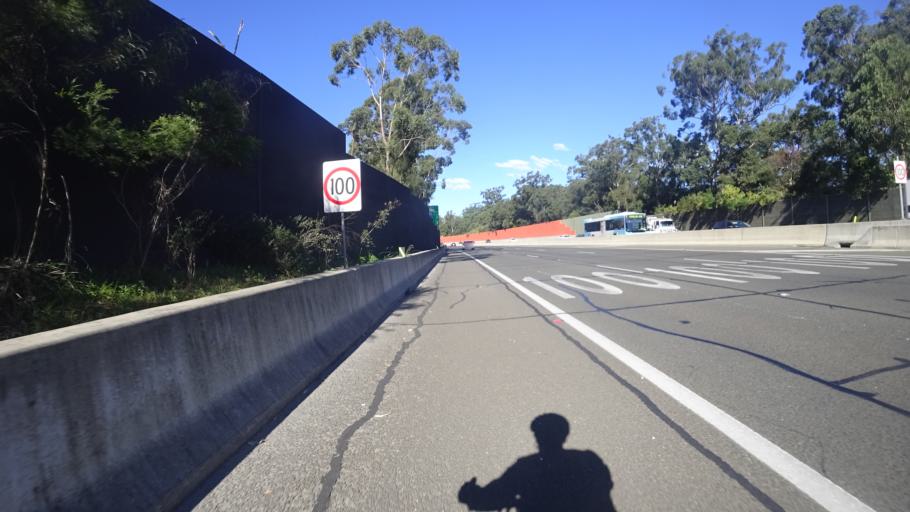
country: AU
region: New South Wales
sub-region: Hornsby Shire
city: Beecroft
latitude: -33.7600
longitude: 151.0679
